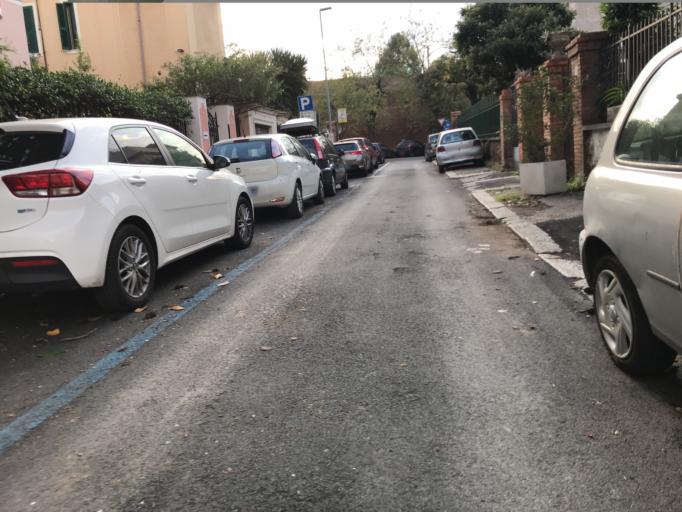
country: IT
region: Latium
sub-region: Citta metropolitana di Roma Capitale
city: Rome
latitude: 41.8996
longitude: 12.5101
